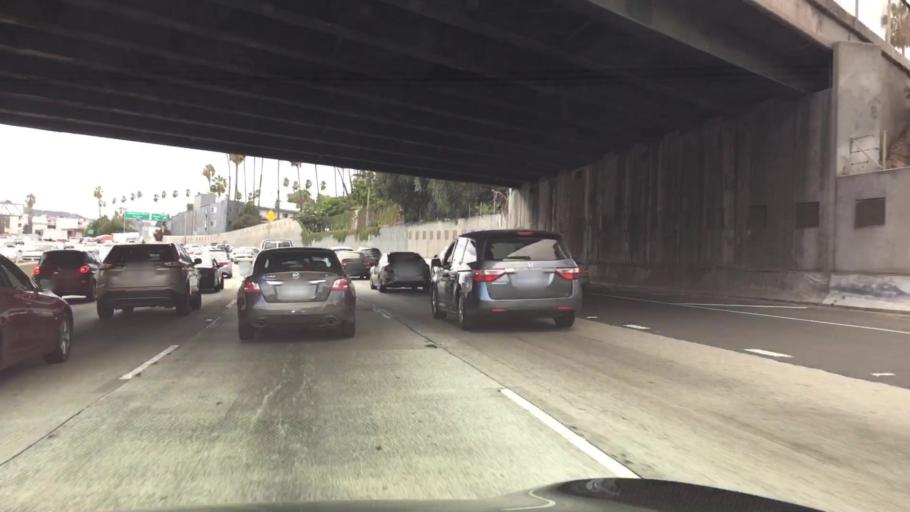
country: US
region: California
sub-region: Los Angeles County
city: Hollywood
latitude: 34.1025
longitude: -118.3195
